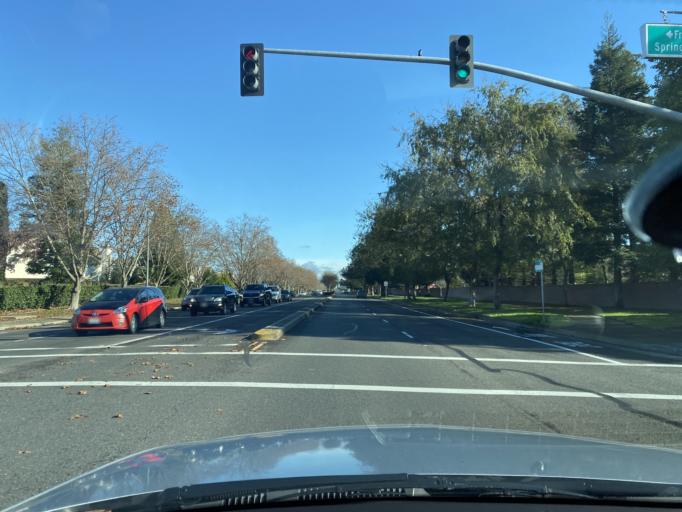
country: US
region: California
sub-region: Sacramento County
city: Elk Grove
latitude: 38.4380
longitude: -121.3798
